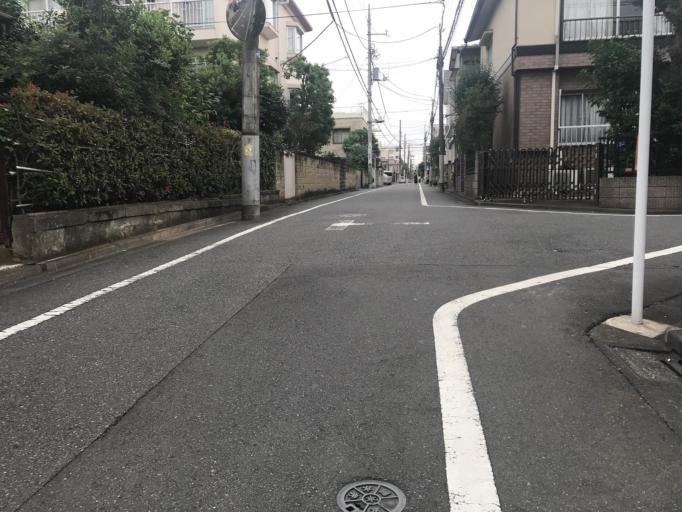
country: JP
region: Tokyo
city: Musashino
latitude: 35.7255
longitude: 139.6150
